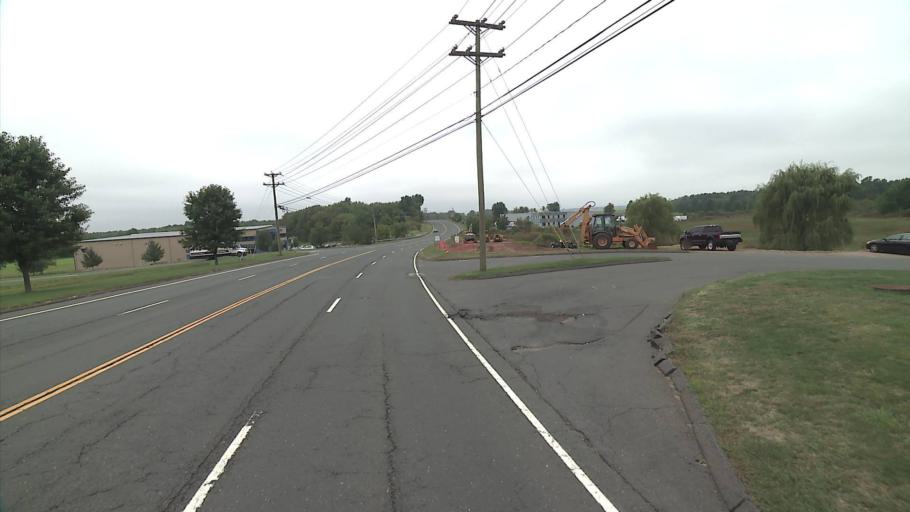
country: US
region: Connecticut
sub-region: Hartford County
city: Suffield Depot
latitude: 41.9597
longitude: -72.6630
